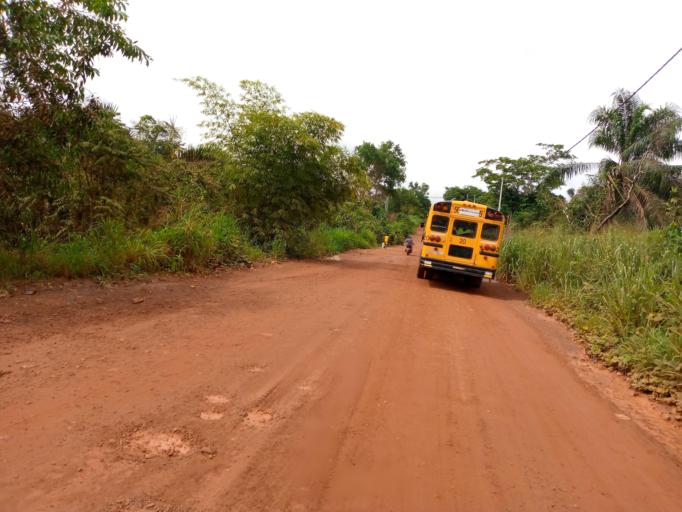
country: SL
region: Southern Province
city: Mogbwemo
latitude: 7.7722
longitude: -12.2964
